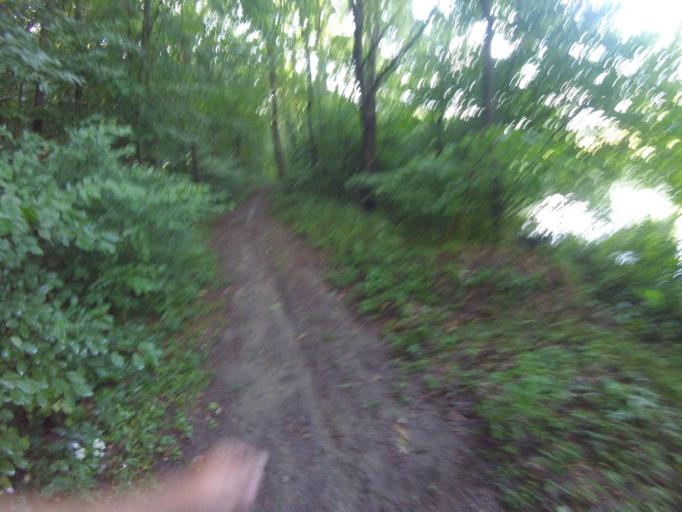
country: HU
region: Zala
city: Becsehely
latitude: 46.4986
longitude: 16.7386
